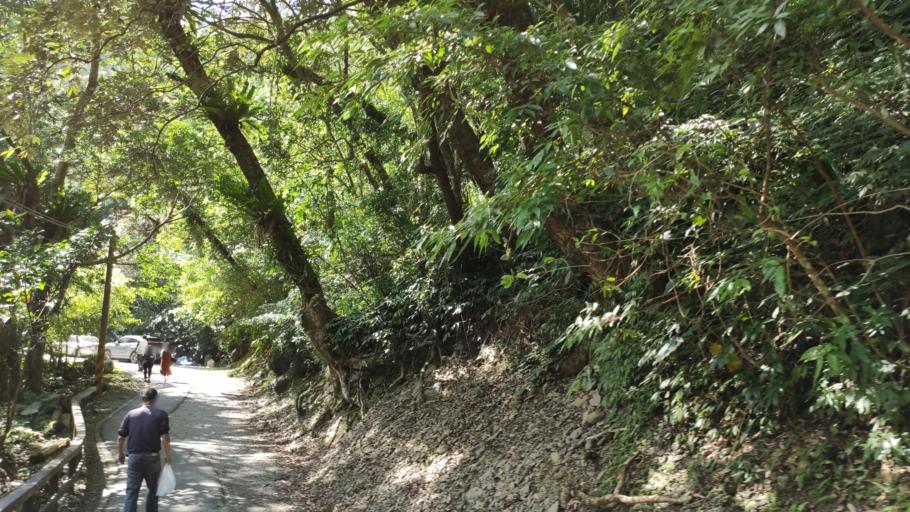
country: TW
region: Taiwan
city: Daxi
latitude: 24.8229
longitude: 121.4491
